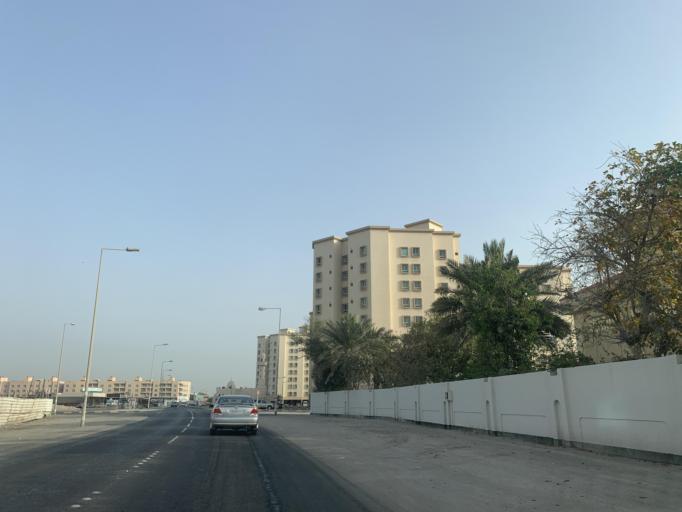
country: BH
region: Northern
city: Madinat `Isa
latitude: 26.1832
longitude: 50.5595
